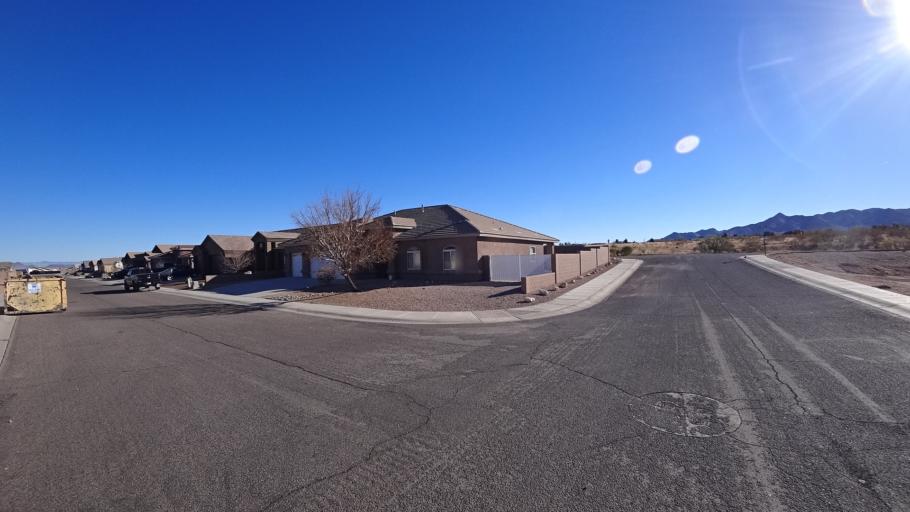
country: US
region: Arizona
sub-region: Mohave County
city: Kingman
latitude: 35.1857
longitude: -113.9988
